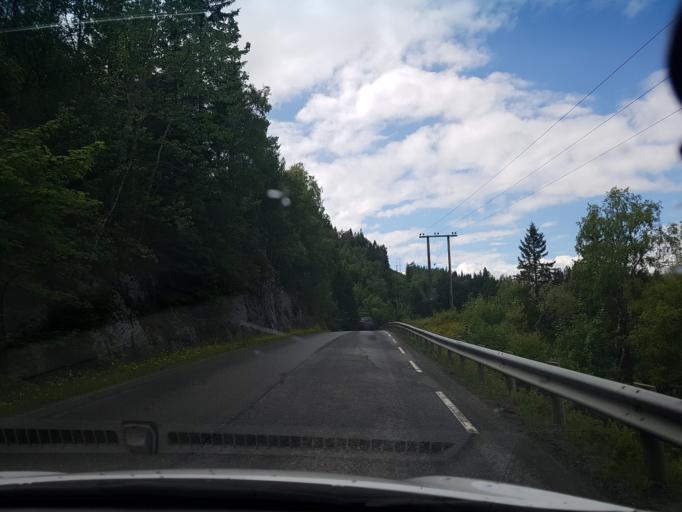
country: NO
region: Nord-Trondelag
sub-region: Stjordal
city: Stjordalshalsen
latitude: 63.6056
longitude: 10.9577
